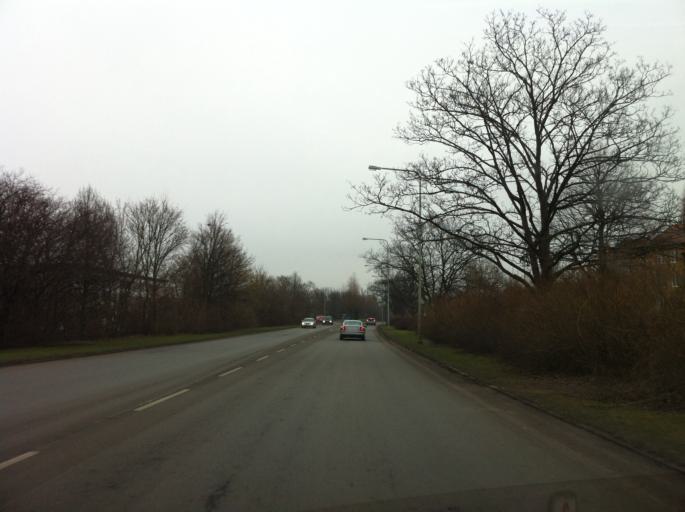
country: SE
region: Skane
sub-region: Landskrona
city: Landskrona
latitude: 55.8858
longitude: 12.8361
